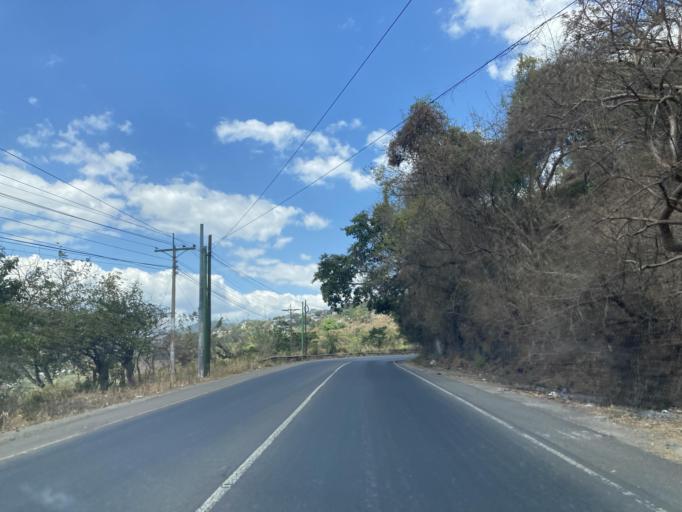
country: GT
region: Santa Rosa
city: Cuilapa
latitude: 14.2647
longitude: -90.2924
